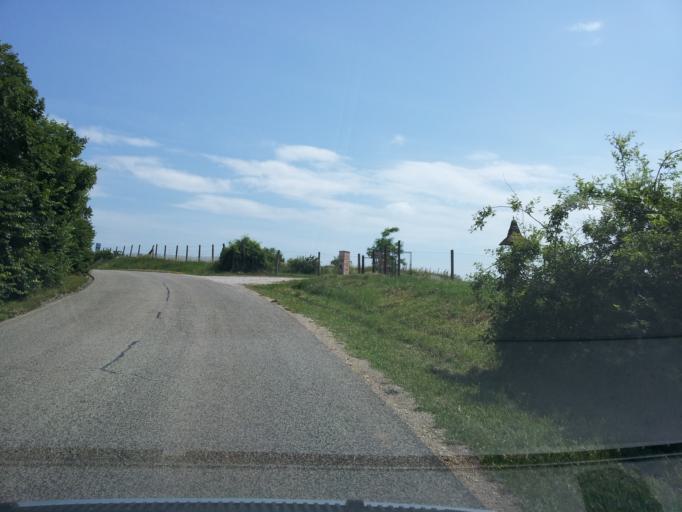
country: HU
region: Veszprem
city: Csopak
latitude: 46.9885
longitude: 17.9514
